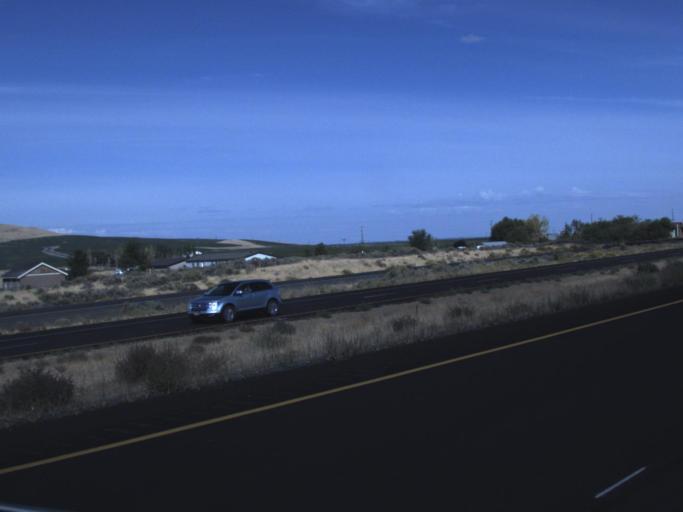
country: US
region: Washington
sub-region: Benton County
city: Benton City
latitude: 46.2572
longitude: -119.4421
